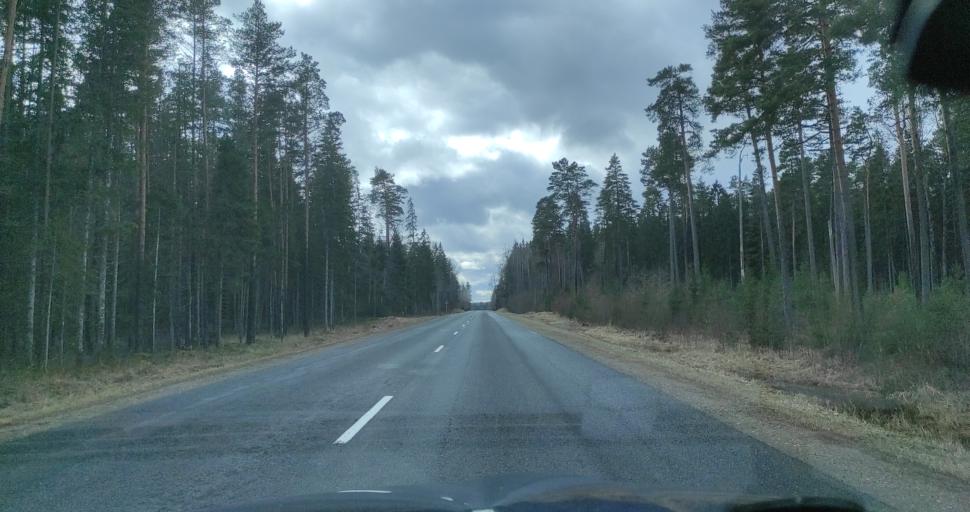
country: LV
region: Talsu Rajons
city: Stende
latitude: 57.0951
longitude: 22.4803
